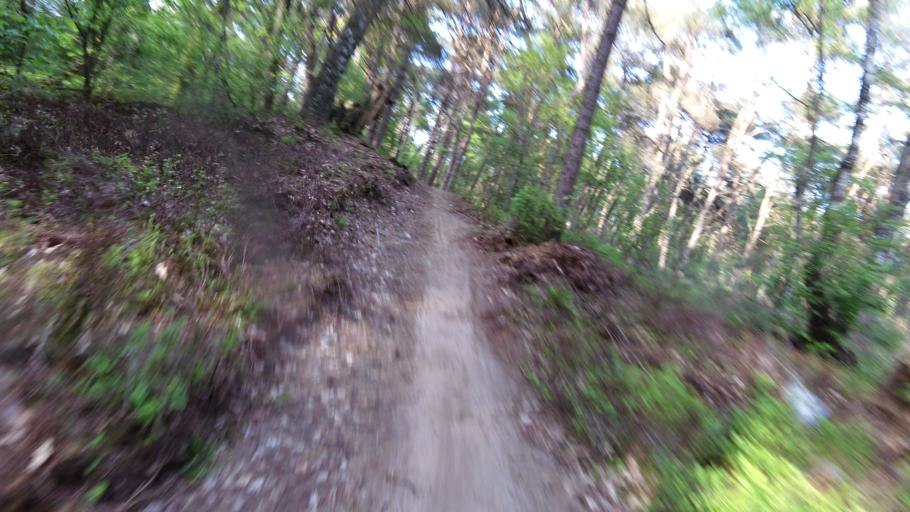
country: NL
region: Gelderland
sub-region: Gemeente Renkum
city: Wolfheze
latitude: 52.0380
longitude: 5.7497
